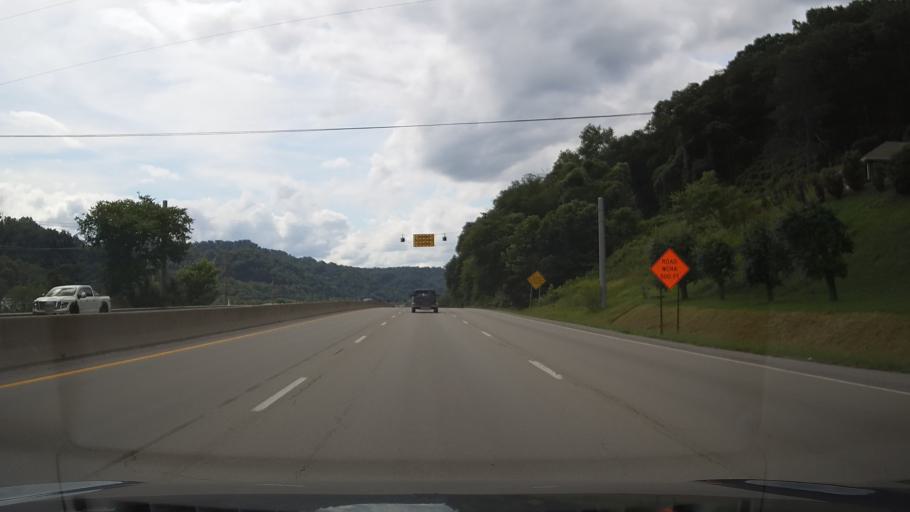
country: US
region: Kentucky
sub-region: Pike County
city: Coal Run Village
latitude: 37.5135
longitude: -82.5559
